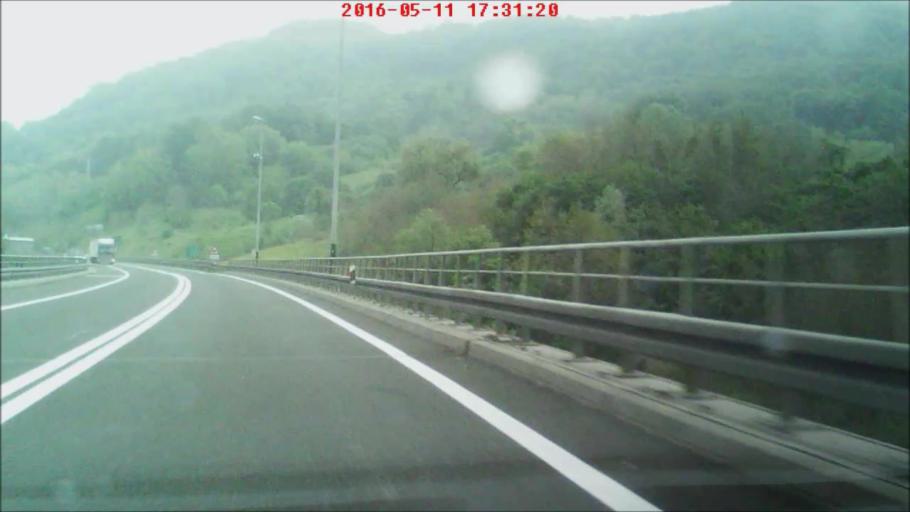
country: HR
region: Krapinsko-Zagorska
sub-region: Grad Krapina
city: Krapina
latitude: 46.1873
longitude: 15.8460
